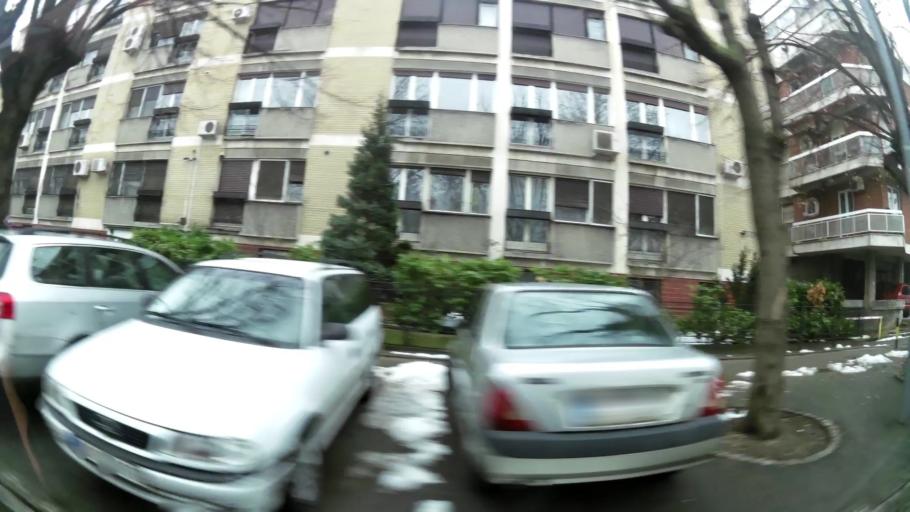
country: RS
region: Central Serbia
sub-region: Belgrade
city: Novi Beograd
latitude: 44.7947
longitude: 20.4408
